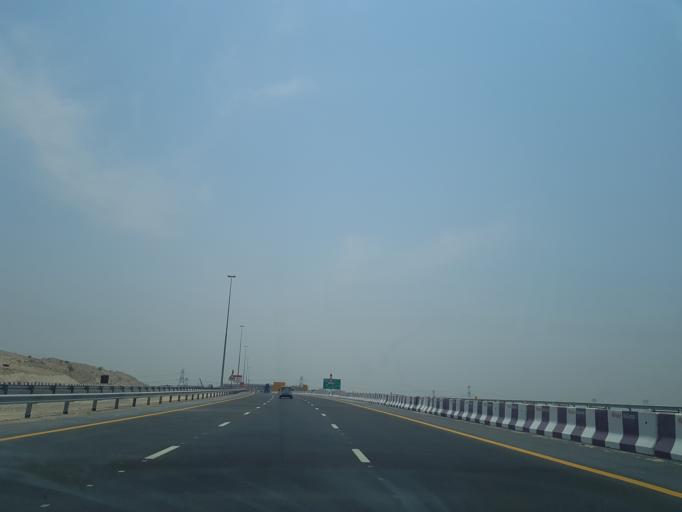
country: AE
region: Dubai
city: Dubai
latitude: 25.0028
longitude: 55.1907
